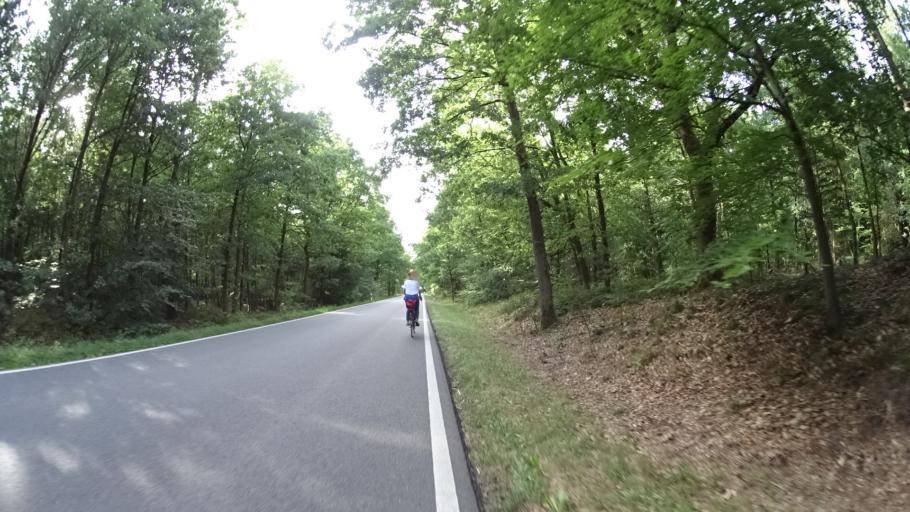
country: DE
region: Lower Saxony
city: Handeloh
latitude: 53.1741
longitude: 9.8888
